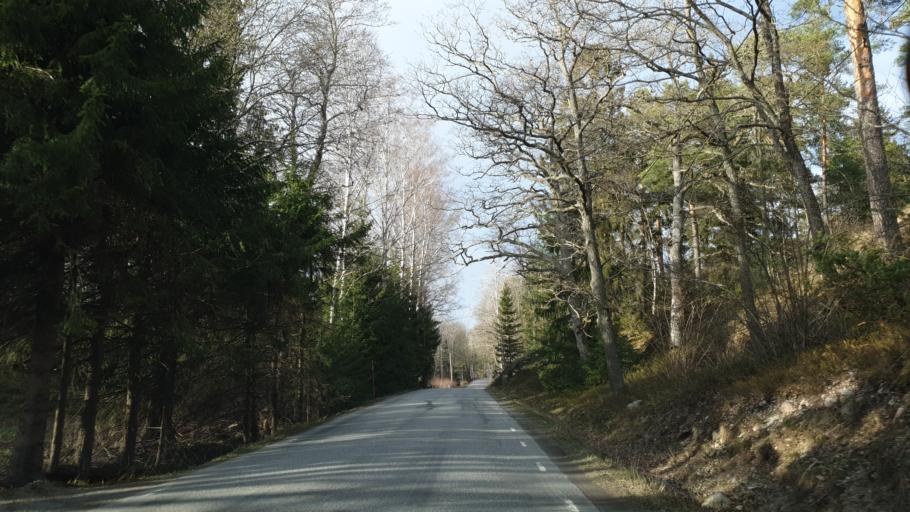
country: SE
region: Stockholm
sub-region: Varmdo Kommun
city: Holo
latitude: 59.3614
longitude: 18.6704
